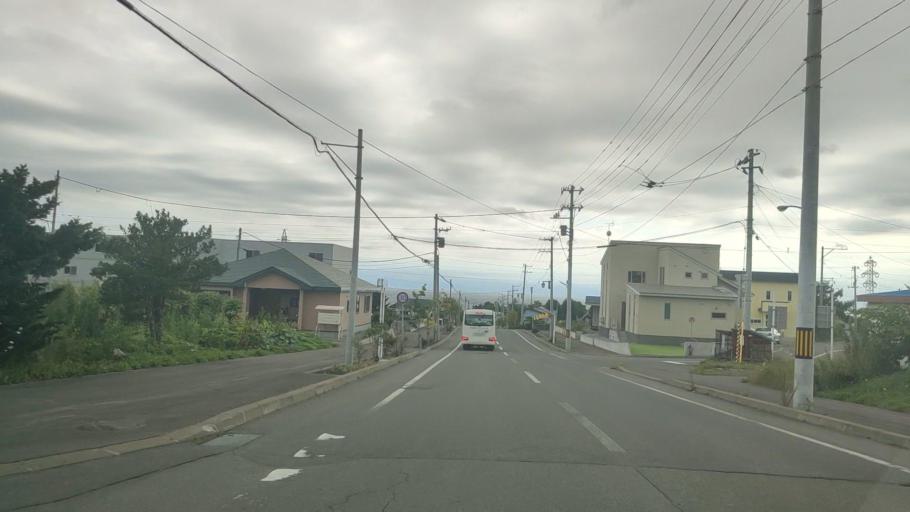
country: JP
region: Hokkaido
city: Date
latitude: 42.5535
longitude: 140.7718
